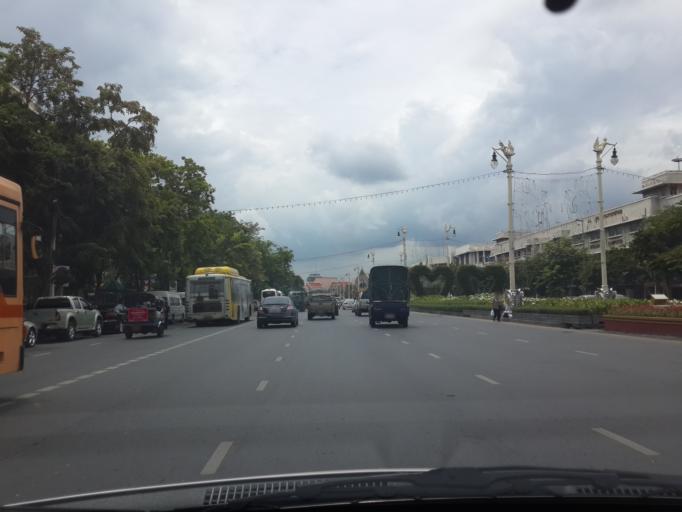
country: TH
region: Bangkok
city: Bangkok
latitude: 13.7566
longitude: 100.5008
